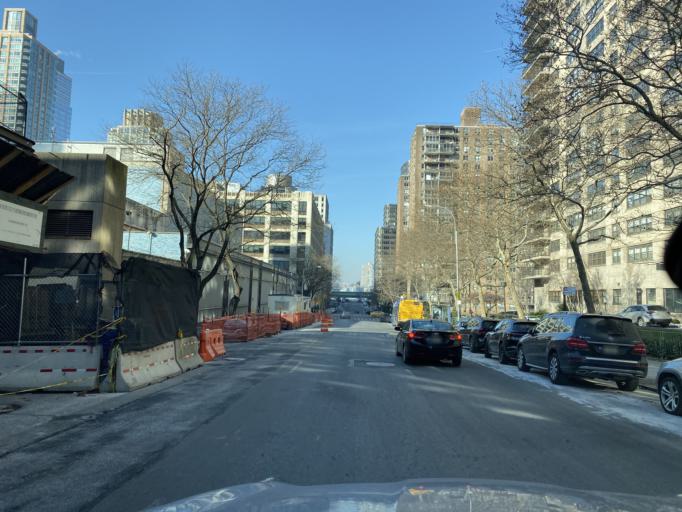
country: US
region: New York
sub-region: New York County
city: Manhattan
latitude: 40.7755
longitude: -73.9859
